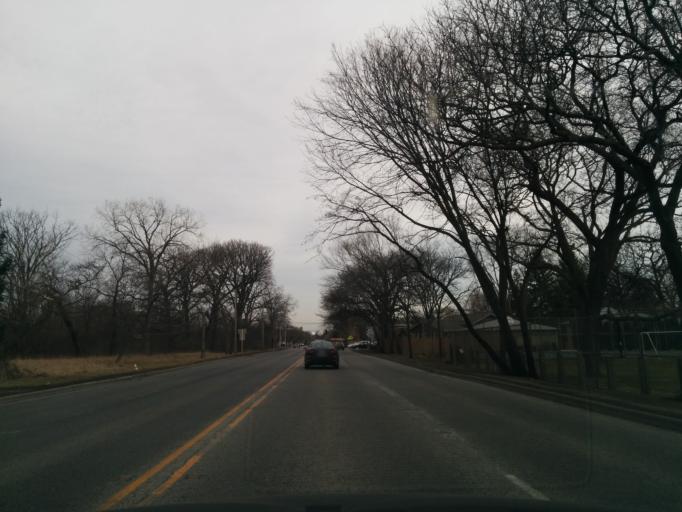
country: US
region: Illinois
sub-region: Cook County
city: Western Springs
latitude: 41.8199
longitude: -87.8923
